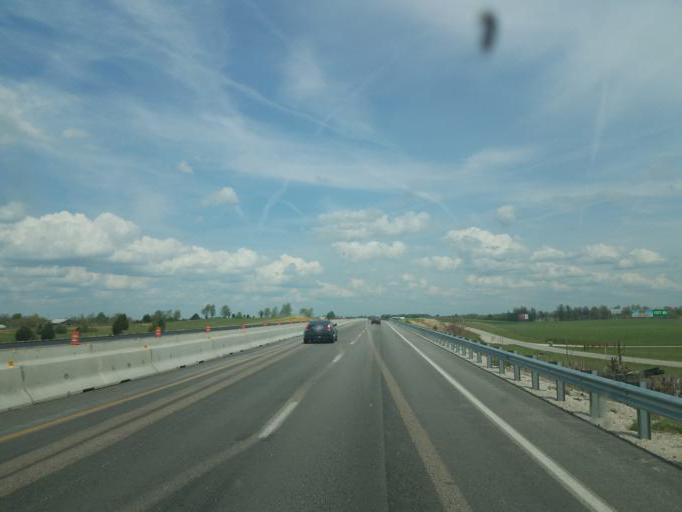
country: US
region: Kentucky
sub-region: Larue County
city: Hodgenville
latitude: 37.4837
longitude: -85.8809
